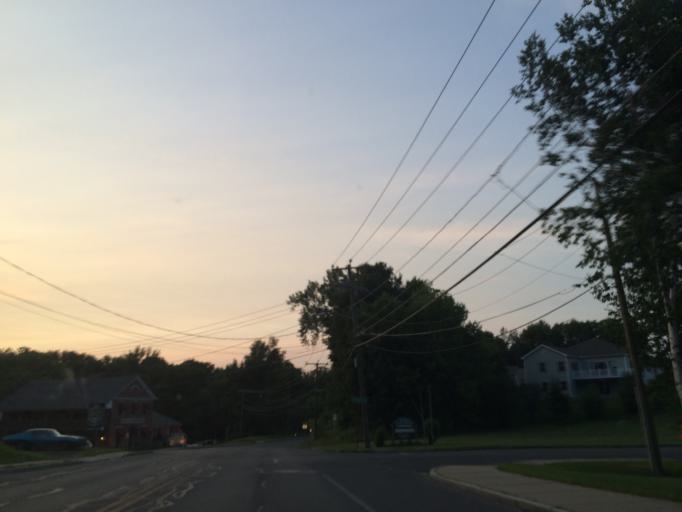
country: US
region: Massachusetts
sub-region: Berkshire County
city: Pittsfield
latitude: 42.4807
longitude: -73.2461
